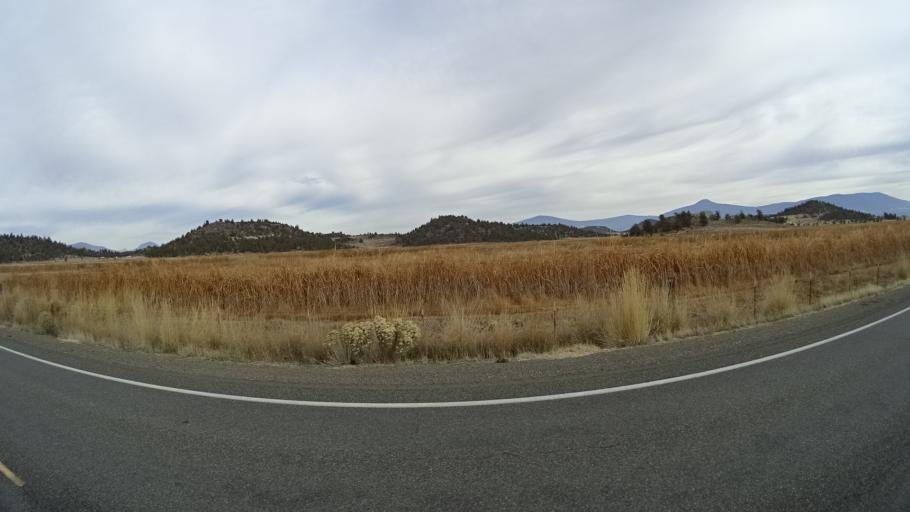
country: US
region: California
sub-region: Siskiyou County
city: Montague
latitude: 41.6452
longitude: -122.4913
